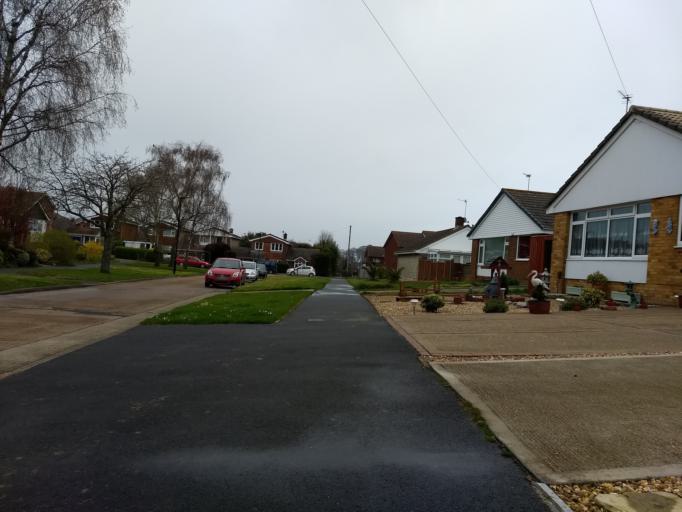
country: GB
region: England
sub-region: Isle of Wight
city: Ryde
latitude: 50.7240
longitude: -1.1895
